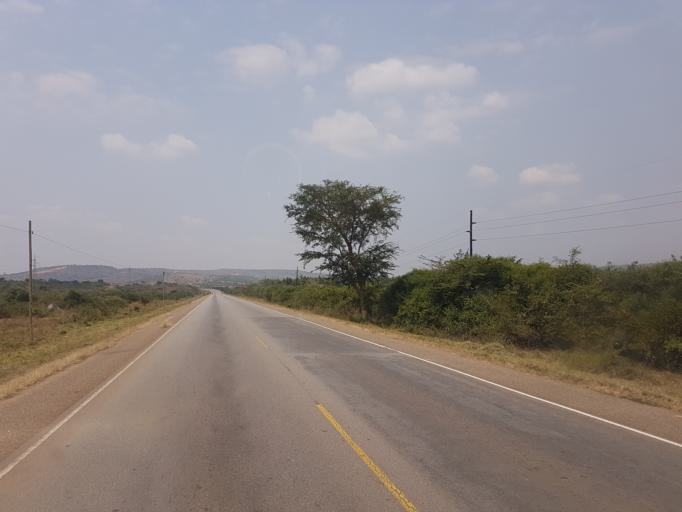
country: UG
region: Western Region
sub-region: Mbarara District
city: Mbarara
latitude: -0.5099
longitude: 30.8321
